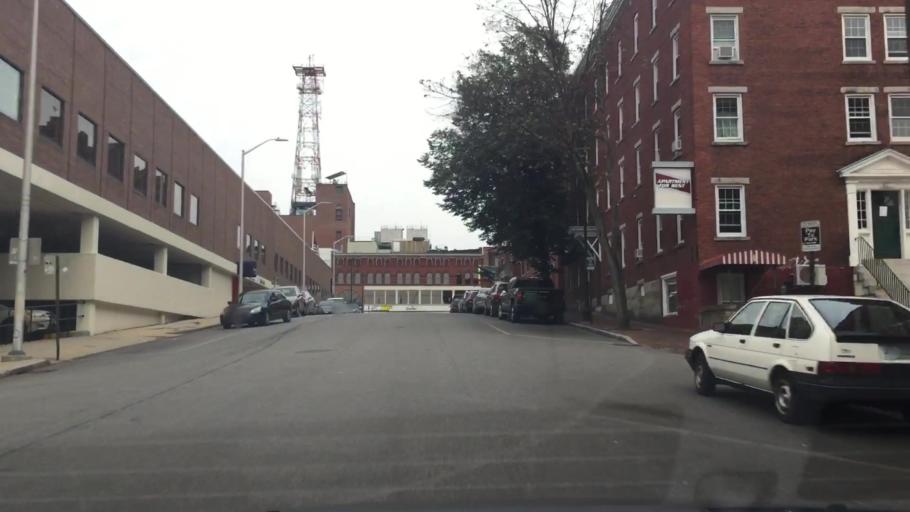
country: US
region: New Hampshire
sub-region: Hillsborough County
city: Manchester
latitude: 42.9922
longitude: -71.4654
